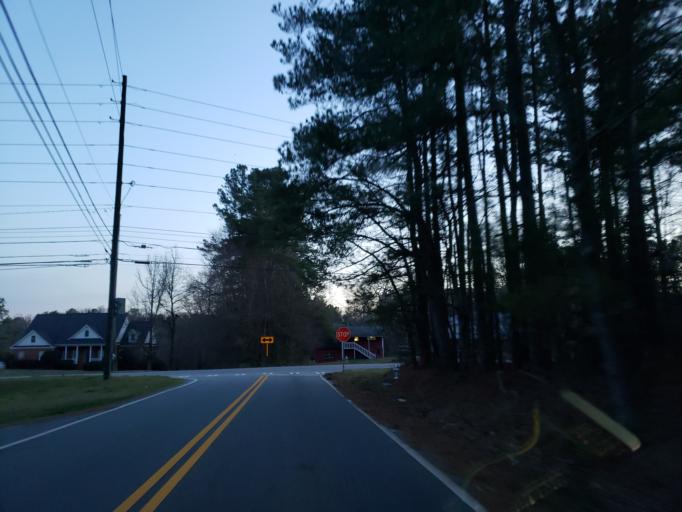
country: US
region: Georgia
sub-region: Cobb County
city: Kennesaw
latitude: 33.9948
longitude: -84.6346
